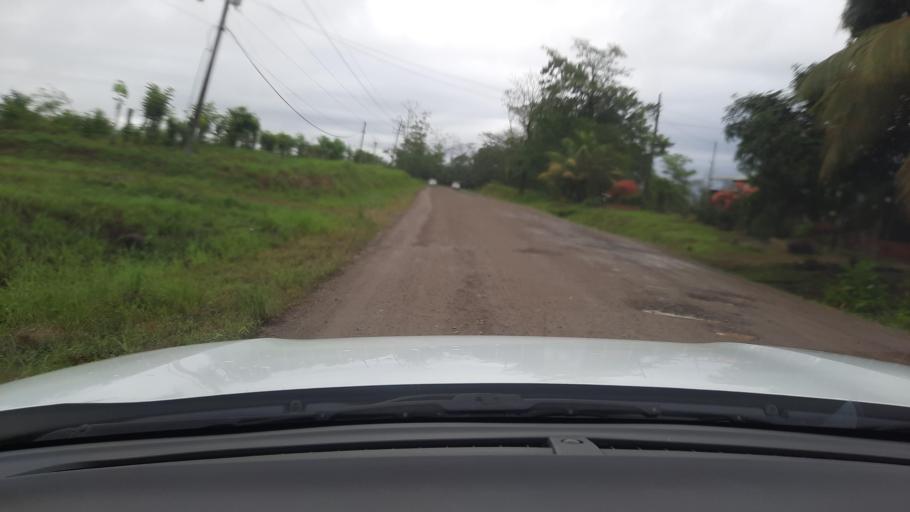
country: CR
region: Alajuela
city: San Jose
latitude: 10.9911
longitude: -85.2758
